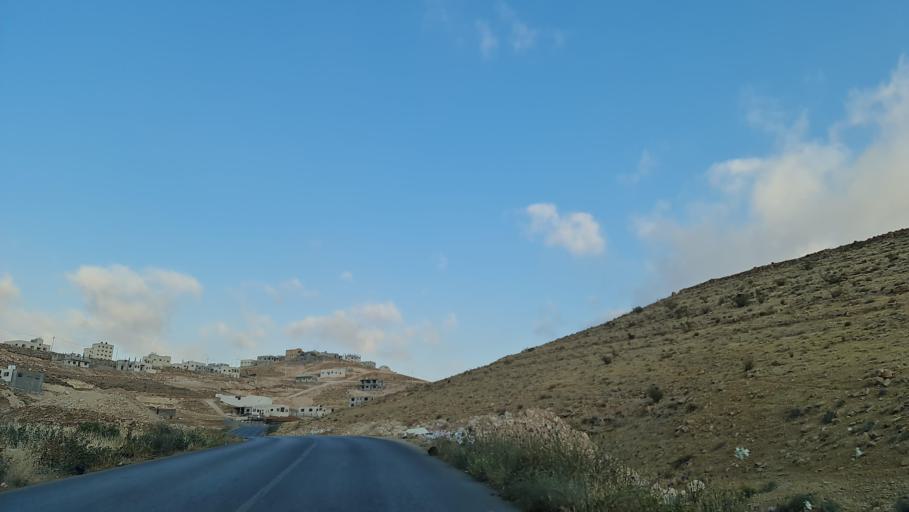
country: JO
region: Zarqa
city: Zarqa
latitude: 32.0819
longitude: 36.0380
